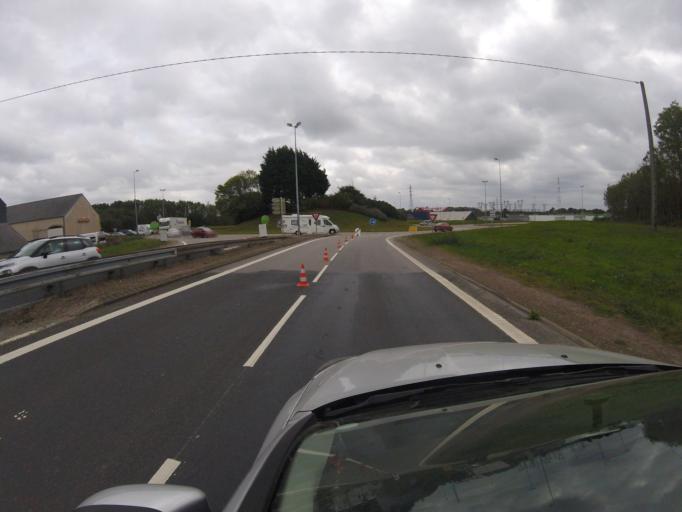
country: FR
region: Lower Normandy
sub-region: Departement de la Manche
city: La Glacerie
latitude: 49.6002
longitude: -1.5976
